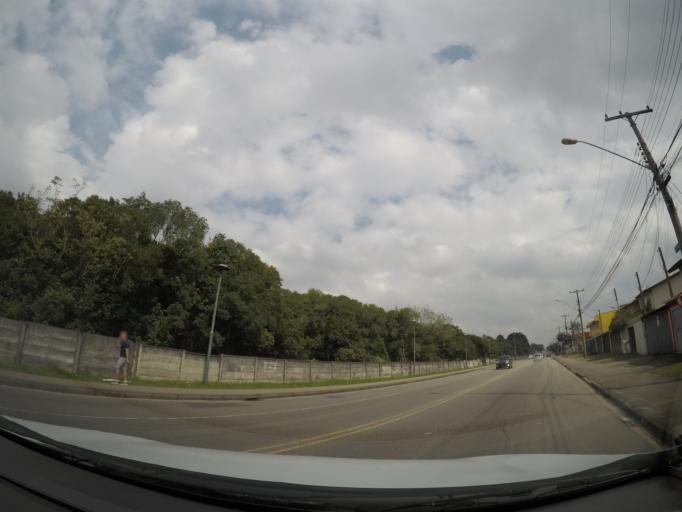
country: BR
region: Parana
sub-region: Sao Jose Dos Pinhais
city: Sao Jose dos Pinhais
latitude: -25.5058
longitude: -49.2437
